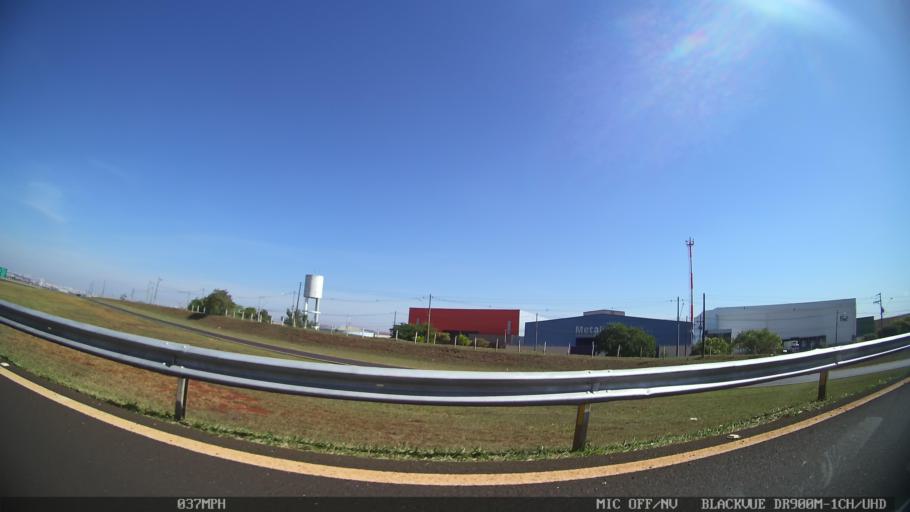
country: BR
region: Sao Paulo
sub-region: Jardinopolis
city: Jardinopolis
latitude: -21.0932
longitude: -47.7958
